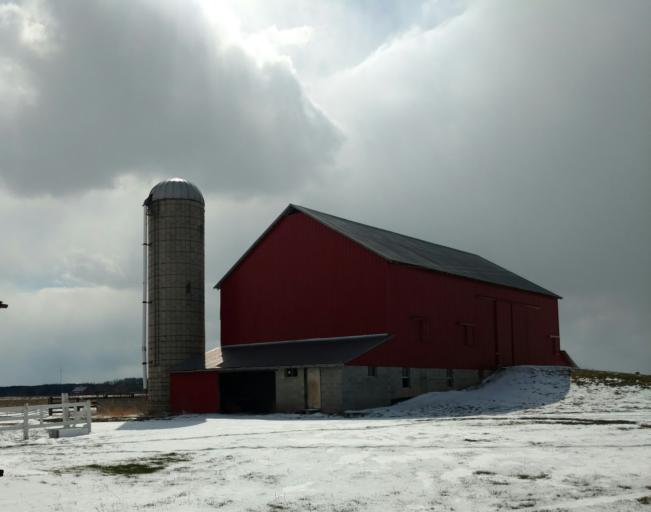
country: US
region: Michigan
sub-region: Gladwin County
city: Gladwin
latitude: 44.0652
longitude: -84.4683
